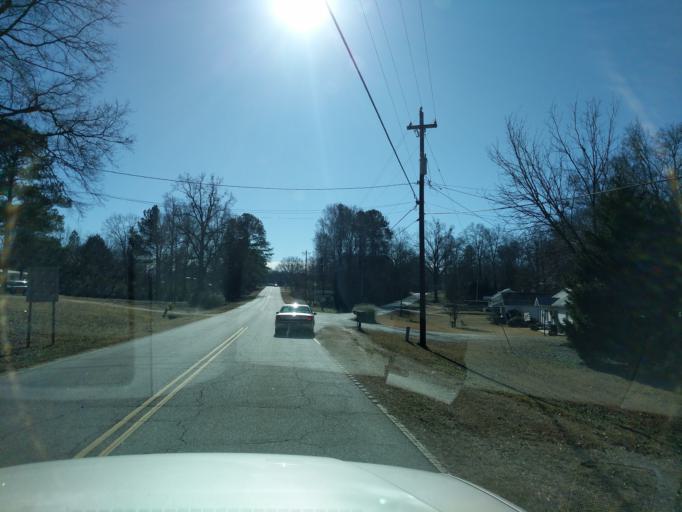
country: US
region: South Carolina
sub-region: Laurens County
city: Clinton
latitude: 34.4901
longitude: -81.8838
